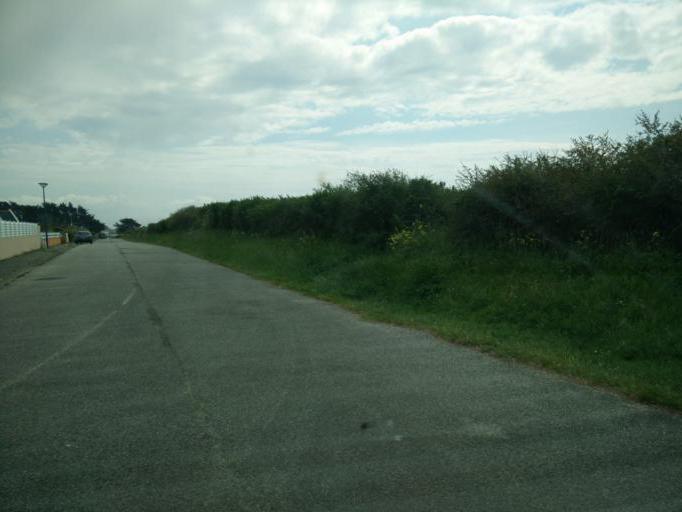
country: FR
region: Brittany
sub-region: Departement du Finistere
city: Camaret-sur-Mer
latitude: 48.2788
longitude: -4.6087
